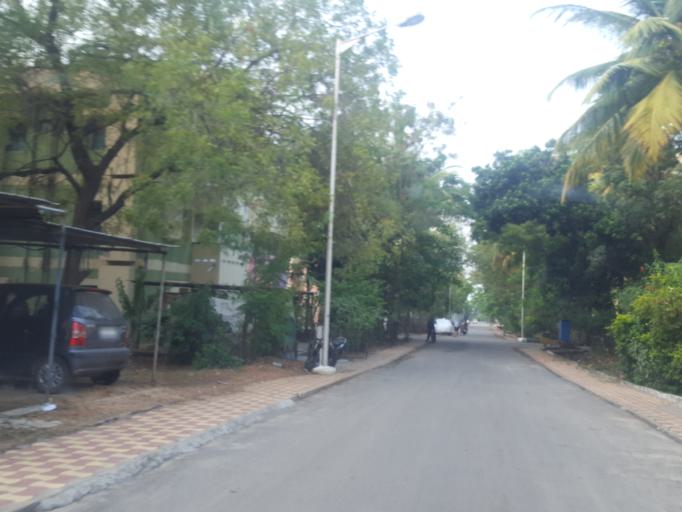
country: IN
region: Telangana
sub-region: Rangareddi
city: Singapur
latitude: 17.4671
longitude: 78.1630
